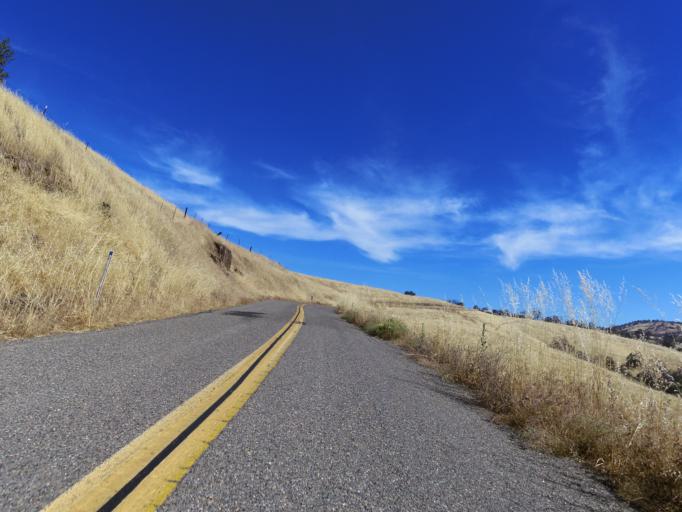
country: US
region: California
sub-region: Mariposa County
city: Mariposa
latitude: 37.3422
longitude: -119.9635
